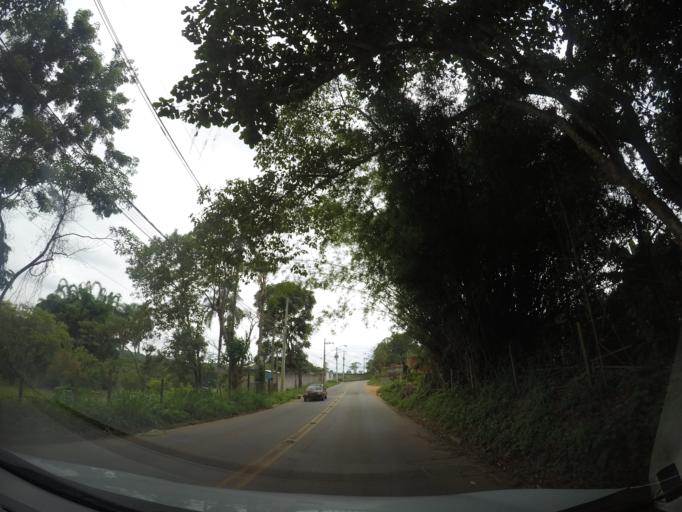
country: BR
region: Sao Paulo
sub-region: Aruja
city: Aruja
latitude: -23.3876
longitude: -46.3964
